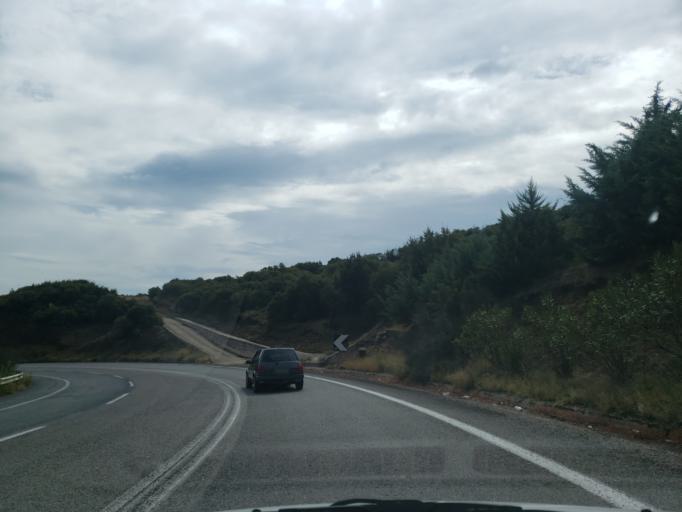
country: GR
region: Central Greece
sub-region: Nomos Fthiotidos
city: Stavros
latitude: 38.9744
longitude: 22.3815
